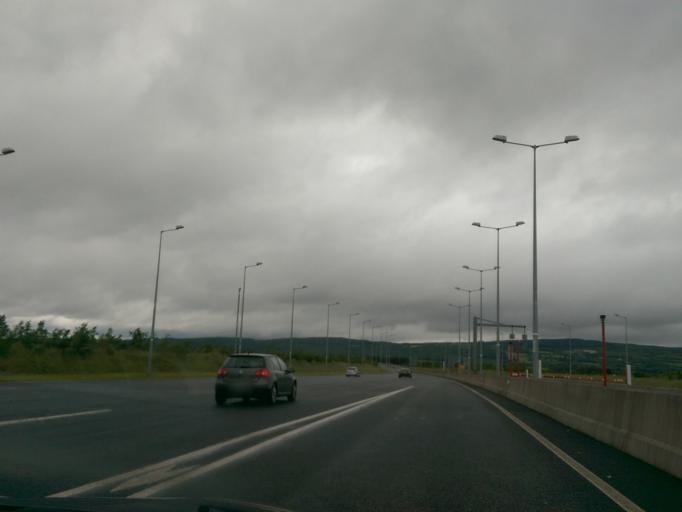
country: IE
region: Munster
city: Moyross
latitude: 52.6702
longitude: -8.7003
